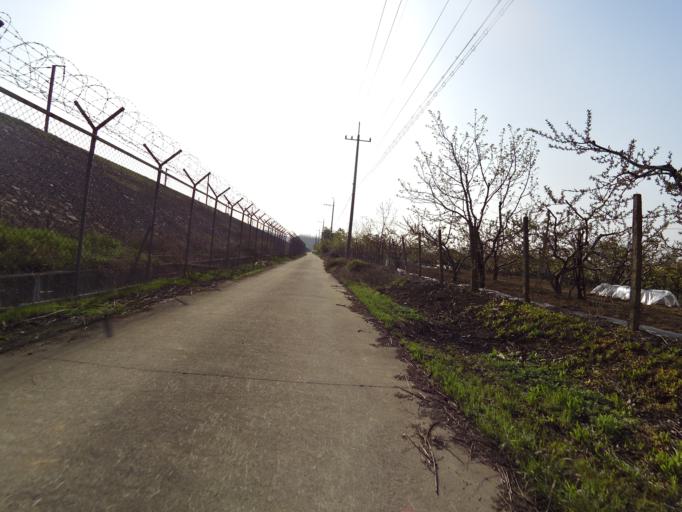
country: KR
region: Gyeongsangbuk-do
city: Gyeongsan-si
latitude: 35.8551
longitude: 128.6999
